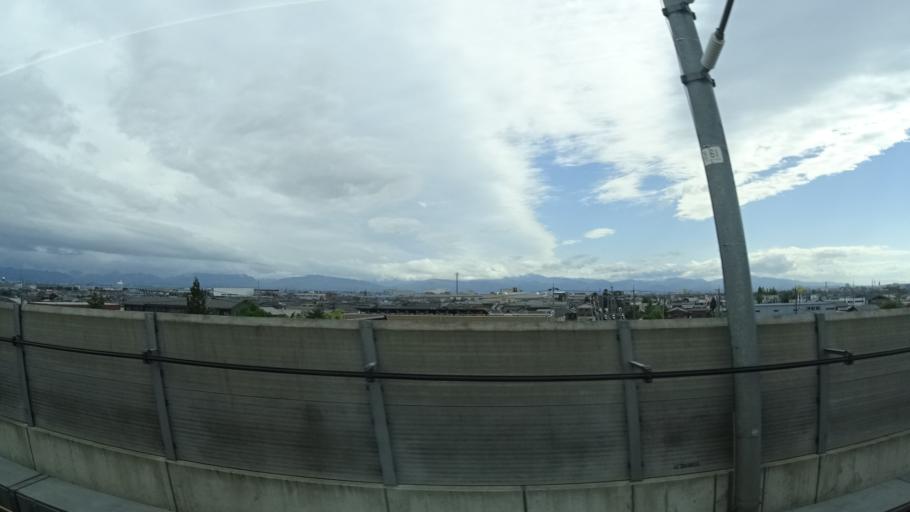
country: JP
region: Toyama
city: Toyama-shi
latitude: 36.7172
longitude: 137.2619
